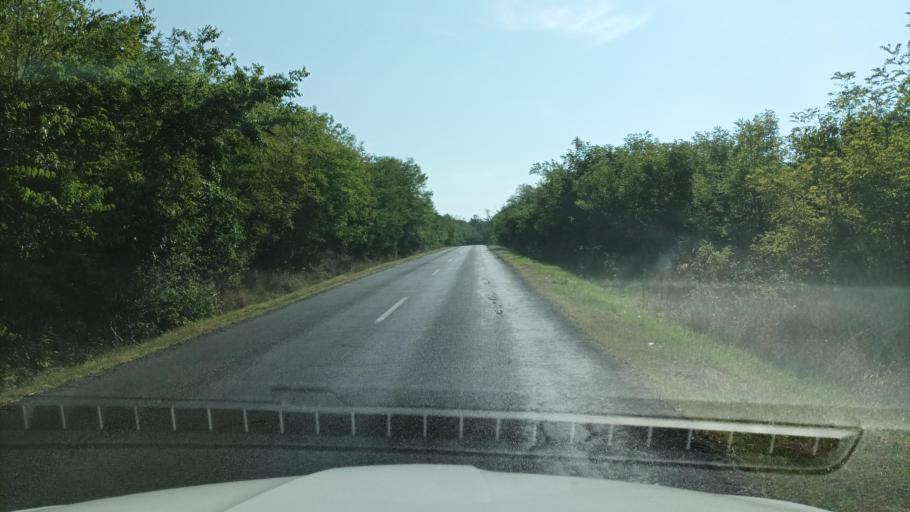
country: HU
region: Pest
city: Isaszeg
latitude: 47.5768
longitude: 19.4256
